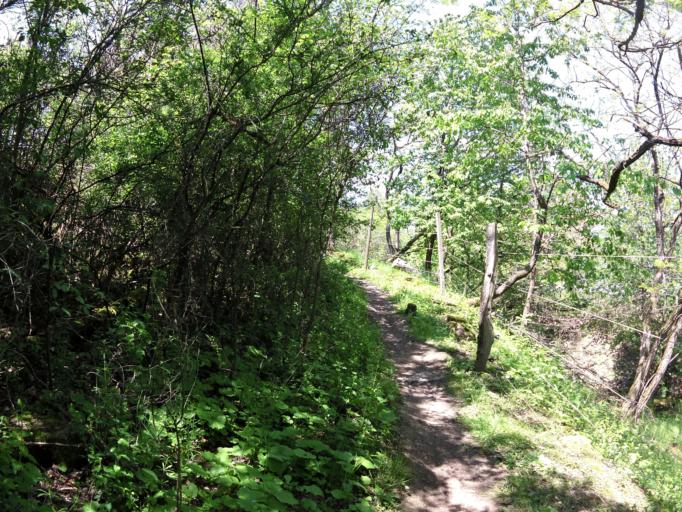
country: DE
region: Bavaria
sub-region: Regierungsbezirk Unterfranken
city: Theilheim
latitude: 49.7373
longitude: 10.0185
